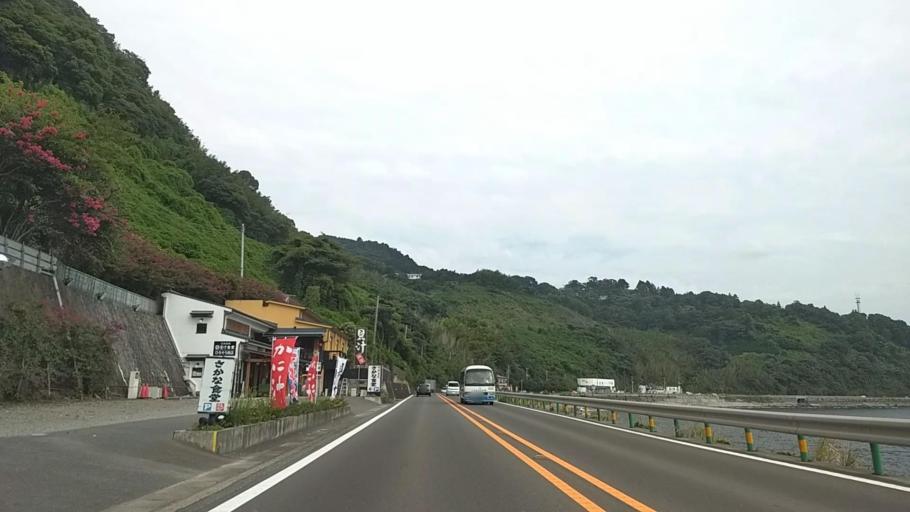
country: JP
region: Kanagawa
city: Yugawara
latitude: 35.1793
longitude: 139.1367
